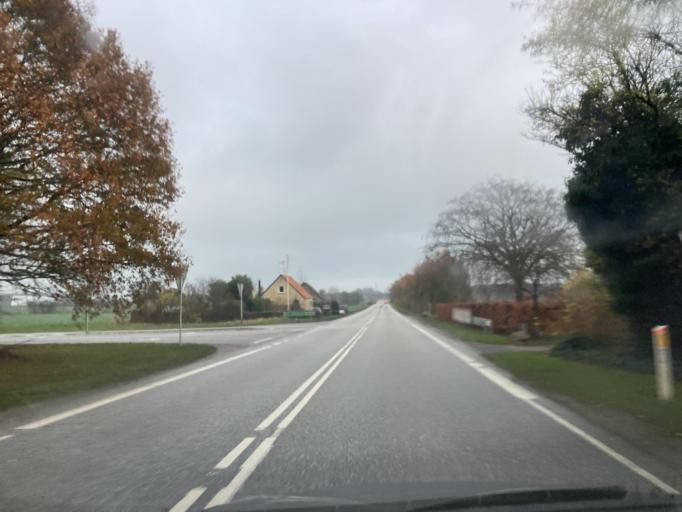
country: DK
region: Zealand
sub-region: Lolland Kommune
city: Holeby
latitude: 54.7158
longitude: 11.4322
